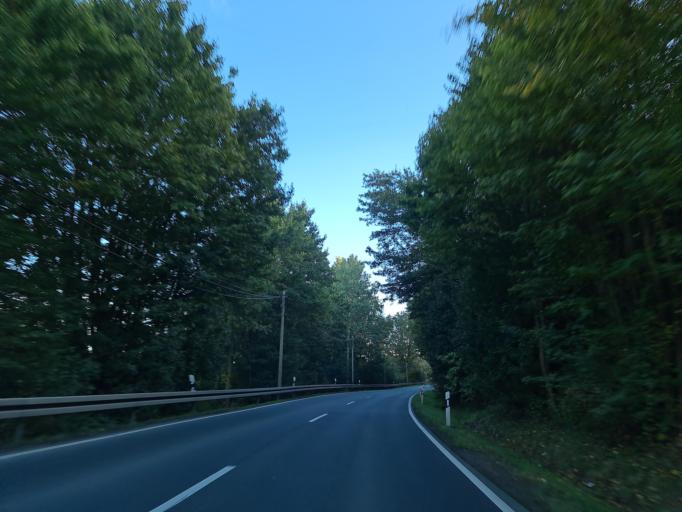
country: DE
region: Thuringia
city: Crimla
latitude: 50.8127
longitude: 12.0750
